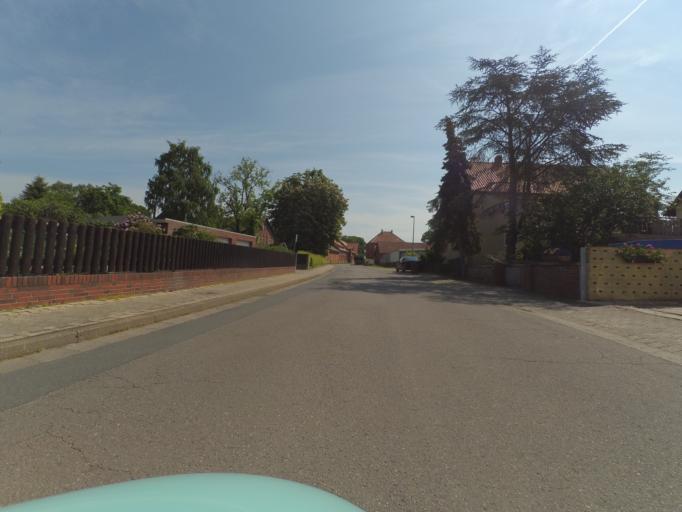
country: DE
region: Lower Saxony
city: Algermissen
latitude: 52.2702
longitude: 10.0123
